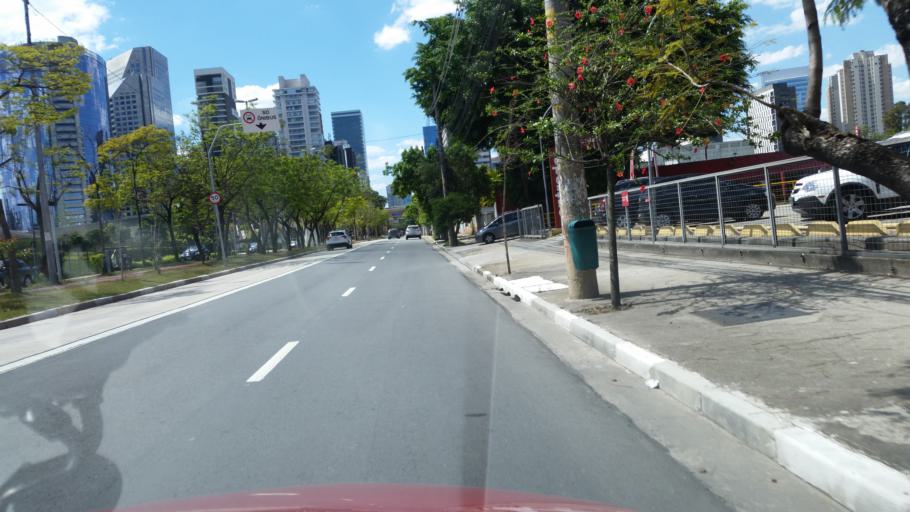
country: BR
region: Sao Paulo
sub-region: Sao Paulo
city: Sao Paulo
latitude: -23.6160
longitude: -46.6967
